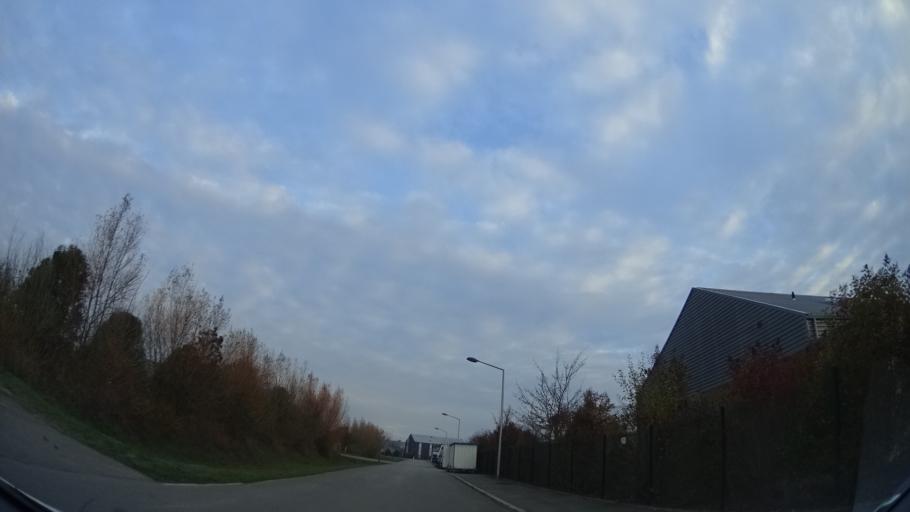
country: FR
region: Brittany
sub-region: Departement d'Ille-et-Vilaine
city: La Chapelle-des-Fougeretz
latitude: 48.1896
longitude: -1.7330
